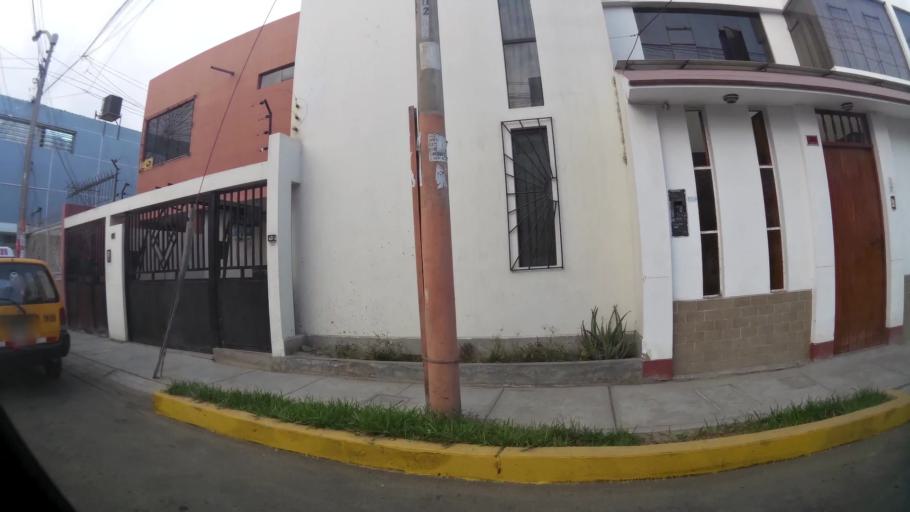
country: PE
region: La Libertad
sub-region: Provincia de Trujillo
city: La Esperanza
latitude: -8.0954
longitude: -79.0381
